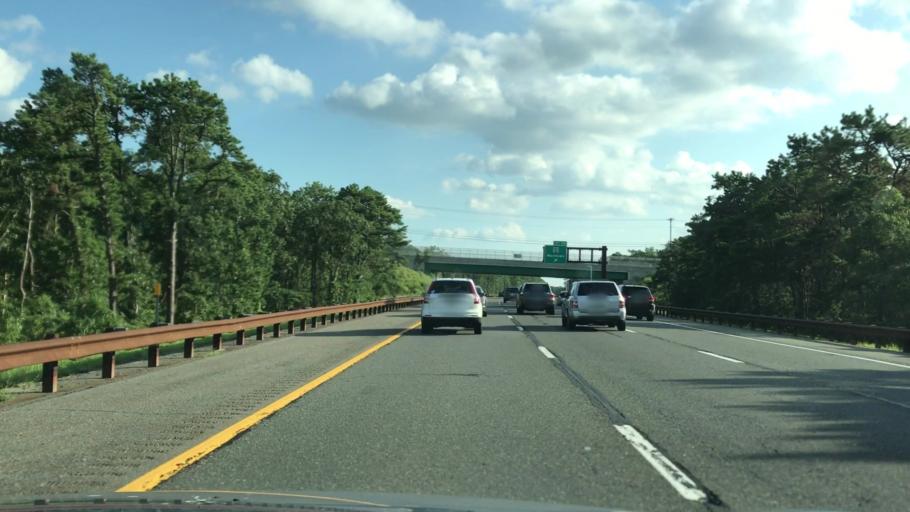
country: US
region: New Jersey
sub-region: Ocean County
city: Waretown
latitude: 39.7973
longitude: -74.2358
